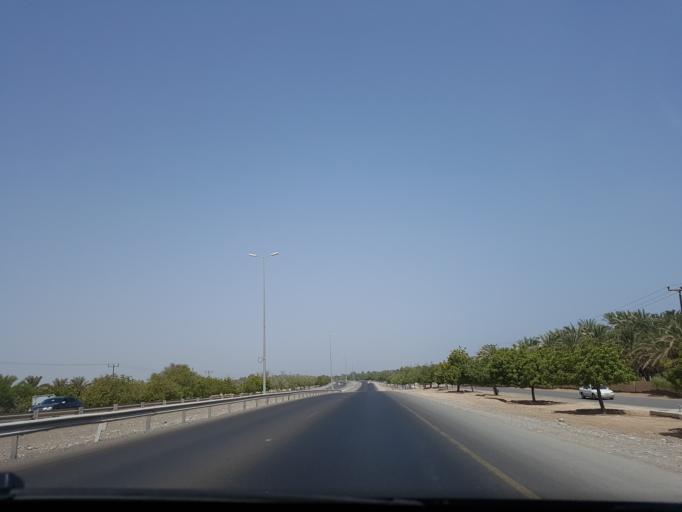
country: OM
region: Al Batinah
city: Al Khaburah
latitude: 24.0311
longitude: 57.0245
